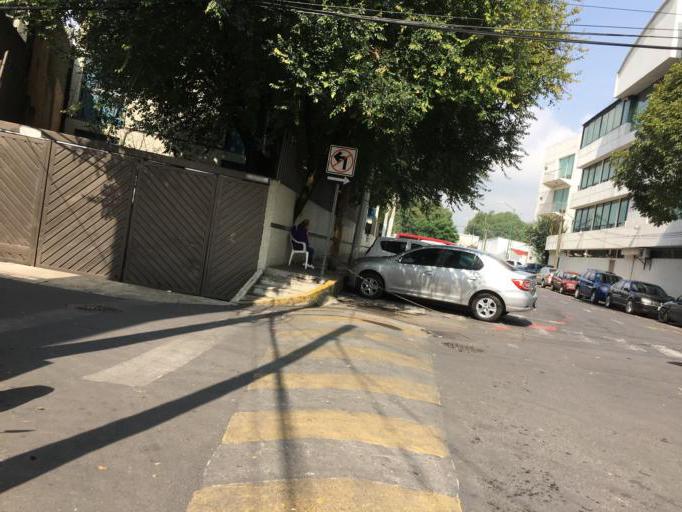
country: MX
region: Mexico City
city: Tlalpan
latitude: 19.2837
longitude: -99.1457
